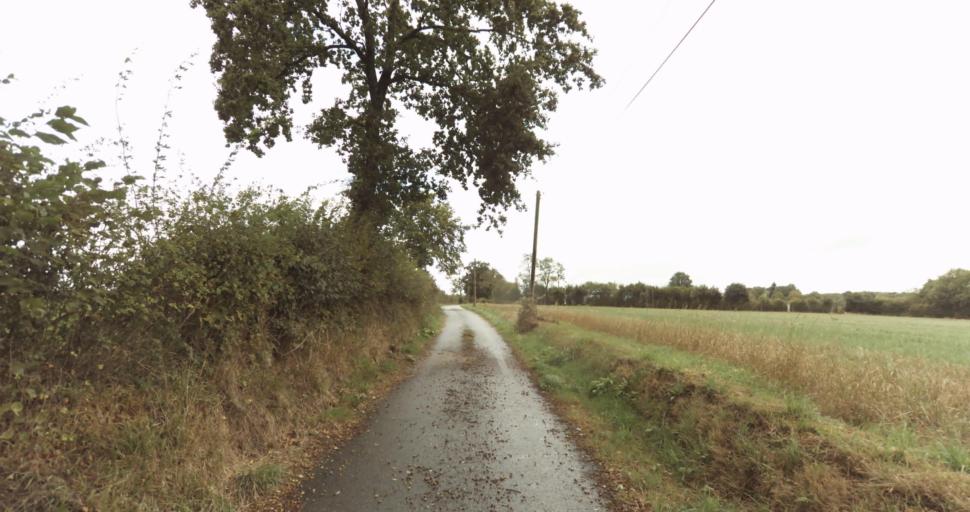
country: FR
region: Lower Normandy
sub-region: Departement de l'Orne
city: Sainte-Gauburge-Sainte-Colombe
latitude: 48.7150
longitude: 0.3841
